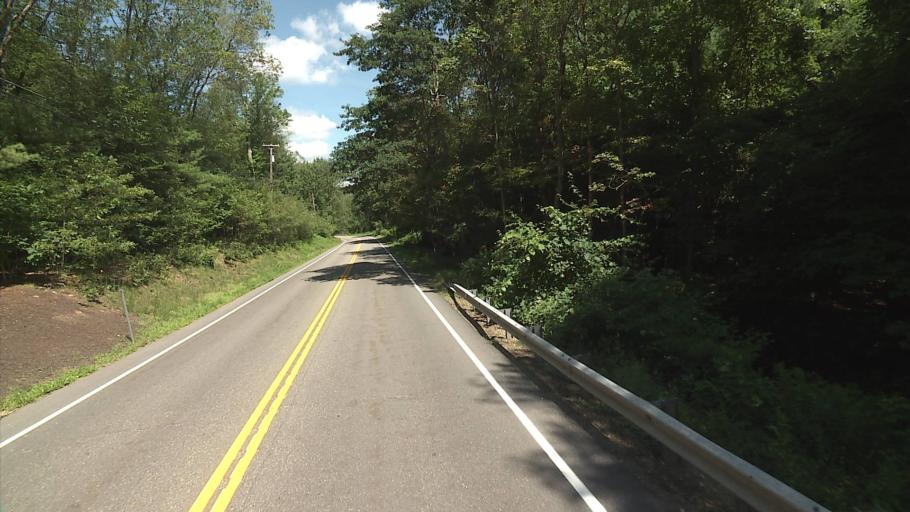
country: US
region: Massachusetts
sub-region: Worcester County
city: Southbridge
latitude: 41.9894
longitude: -72.0815
